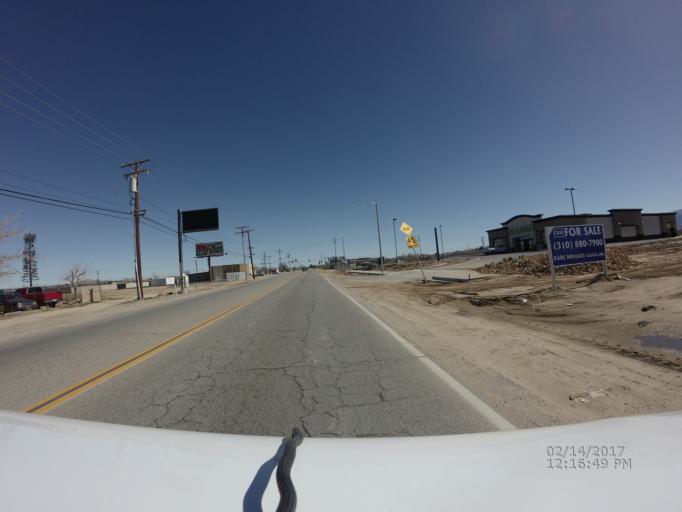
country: US
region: California
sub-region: Los Angeles County
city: Littlerock
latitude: 34.5797
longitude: -117.9713
